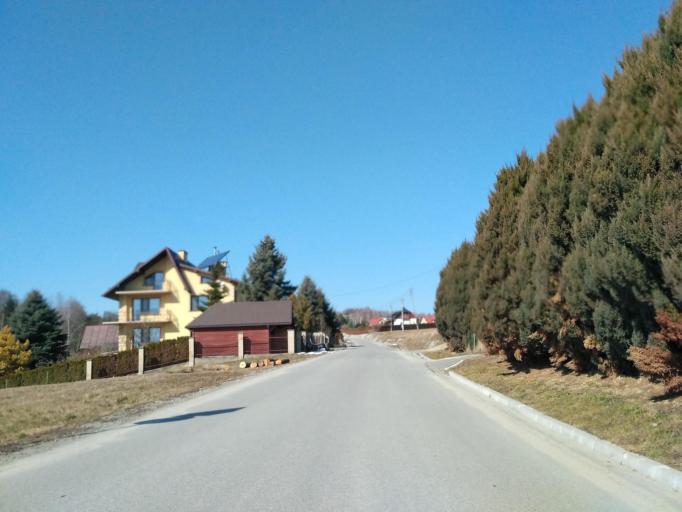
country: PL
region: Subcarpathian Voivodeship
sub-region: Powiat brzozowski
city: Jasienica Rosielna
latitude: 49.7537
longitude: 21.9422
